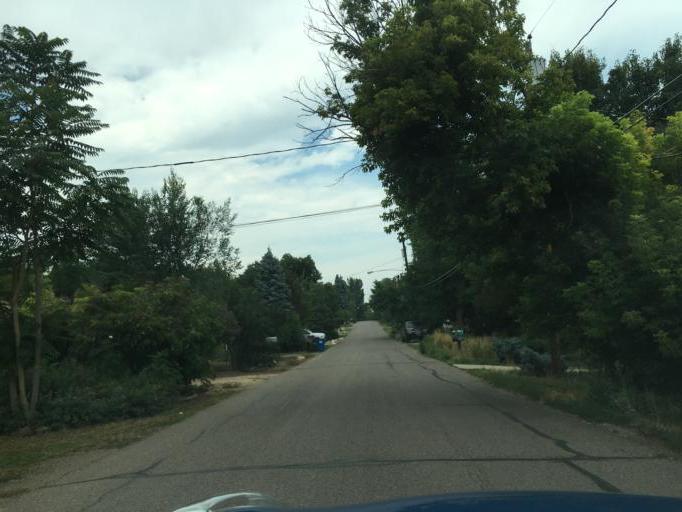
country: US
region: Colorado
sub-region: Jefferson County
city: Wheat Ridge
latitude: 39.7493
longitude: -105.0983
